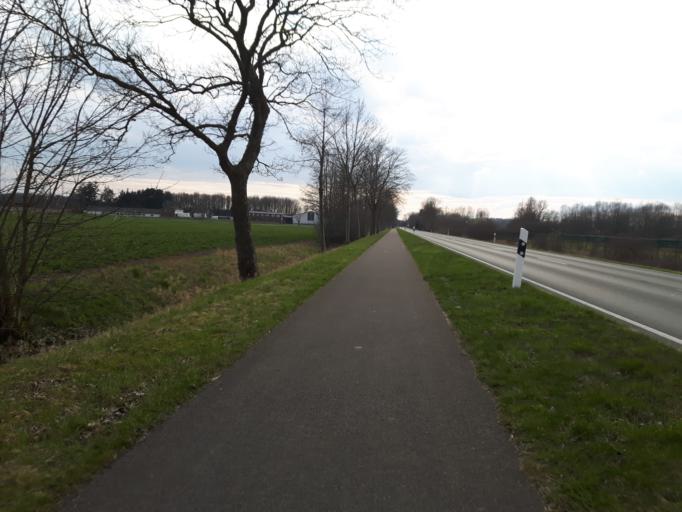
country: DE
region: North Rhine-Westphalia
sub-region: Regierungsbezirk Munster
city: Senden
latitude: 51.9022
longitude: 7.4390
